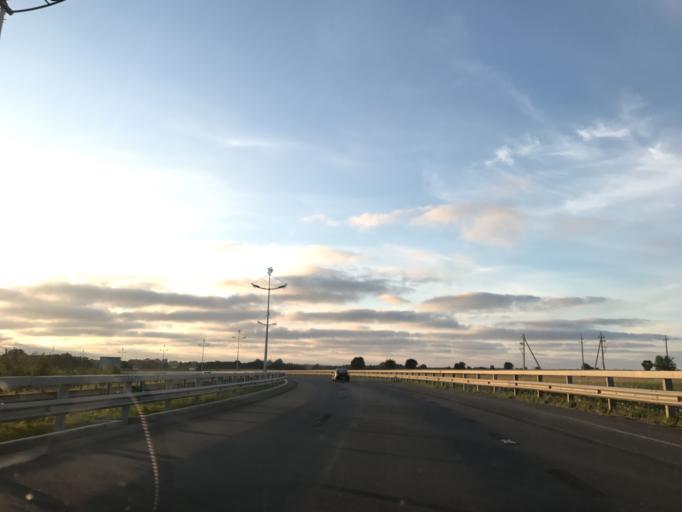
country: RU
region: Kaliningrad
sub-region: Gorod Kaliningrad
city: Pionerskiy
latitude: 54.9123
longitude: 20.2005
